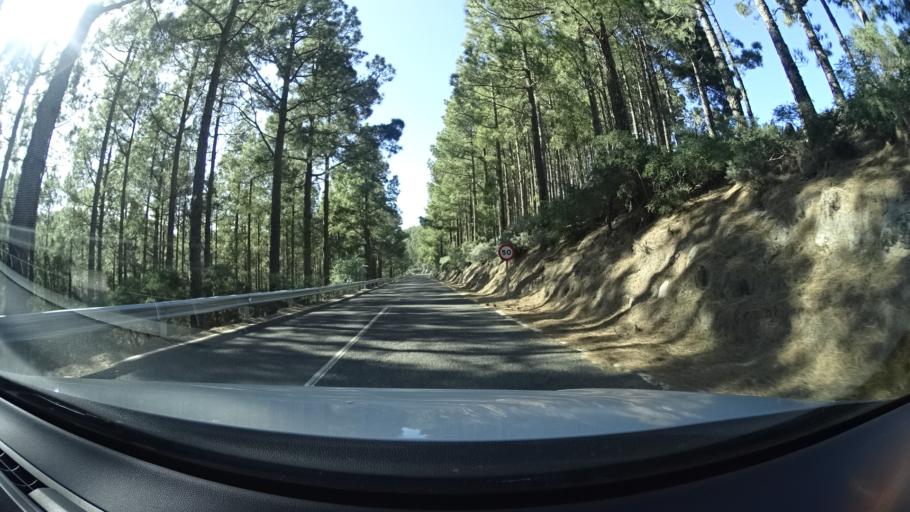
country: ES
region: Canary Islands
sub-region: Provincia de Las Palmas
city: Vega de San Mateo
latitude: 27.9652
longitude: -15.5424
